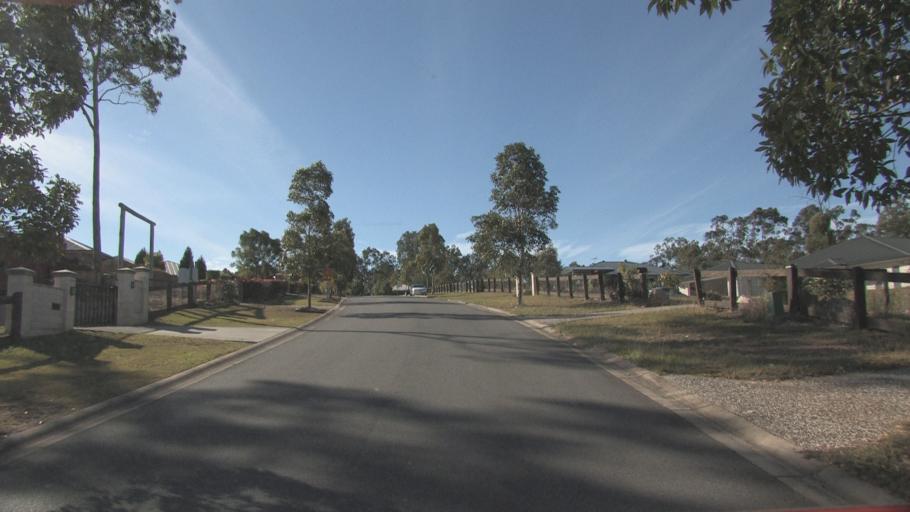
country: AU
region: Queensland
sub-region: Ipswich
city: Springfield Lakes
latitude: -27.7244
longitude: 152.9244
